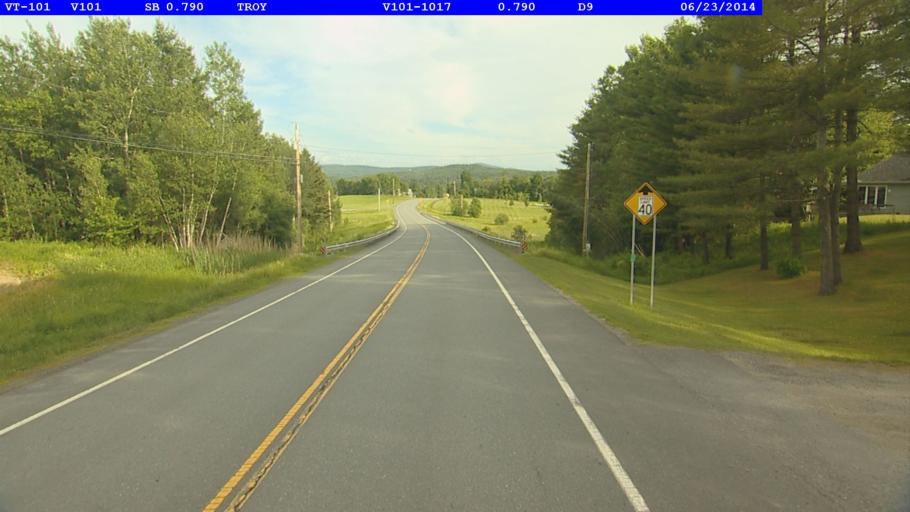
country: US
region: Vermont
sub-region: Orleans County
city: Newport
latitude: 44.9145
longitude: -72.4077
